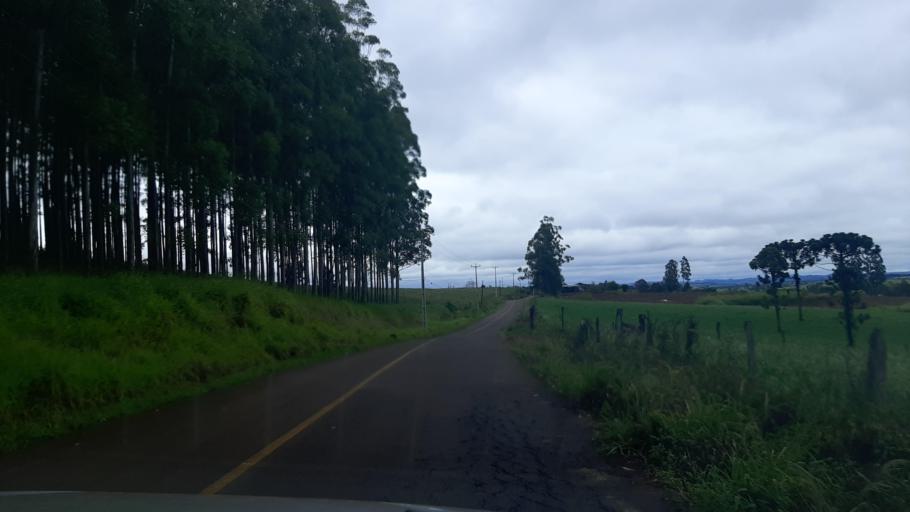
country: BR
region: Parana
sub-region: Ampere
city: Ampere
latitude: -26.0389
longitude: -53.5023
